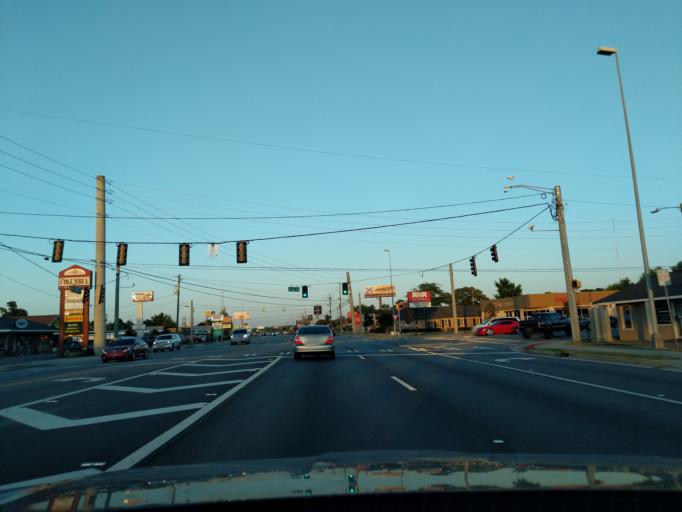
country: US
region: Georgia
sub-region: Columbia County
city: Martinez
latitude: 33.5129
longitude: -82.0868
